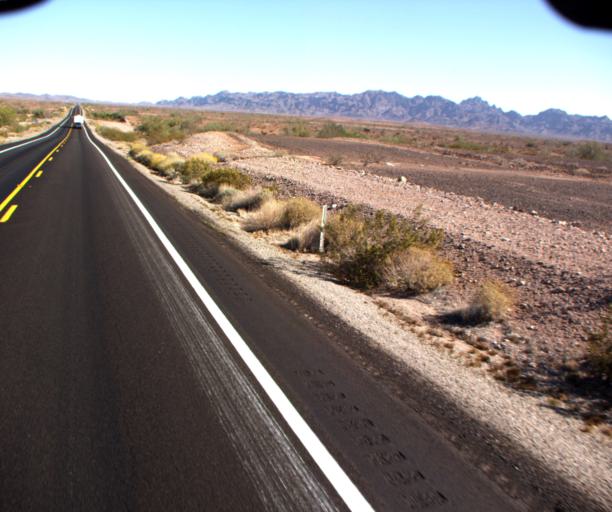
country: US
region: Arizona
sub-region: Yuma County
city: Wellton
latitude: 33.1184
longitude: -114.2928
